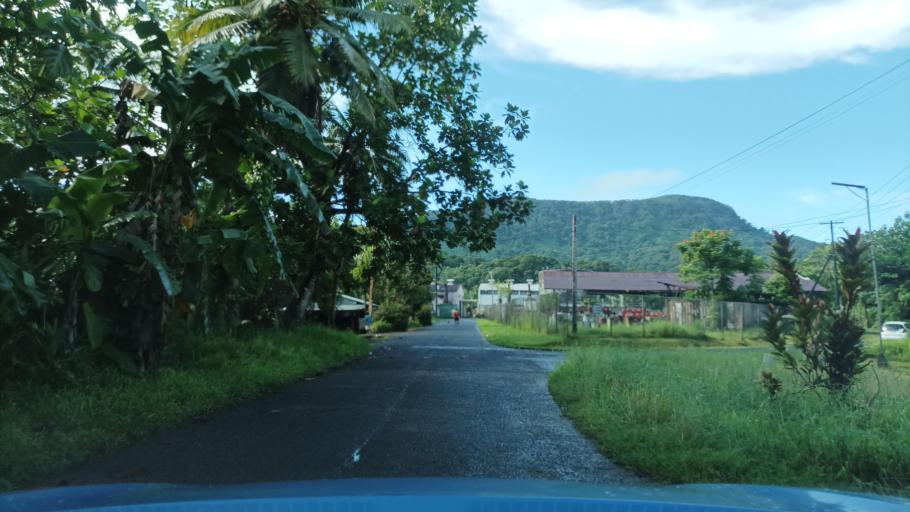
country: FM
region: Pohnpei
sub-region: Kolonia Municipality
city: Kolonia Town
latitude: 6.9365
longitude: 158.1917
